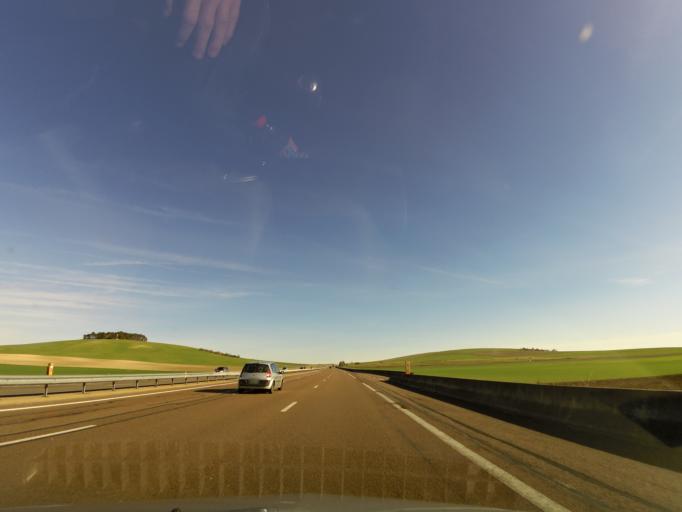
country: FR
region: Bourgogne
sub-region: Departement de l'Yonne
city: Aillant-sur-Tholon
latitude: 47.8977
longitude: 3.3709
